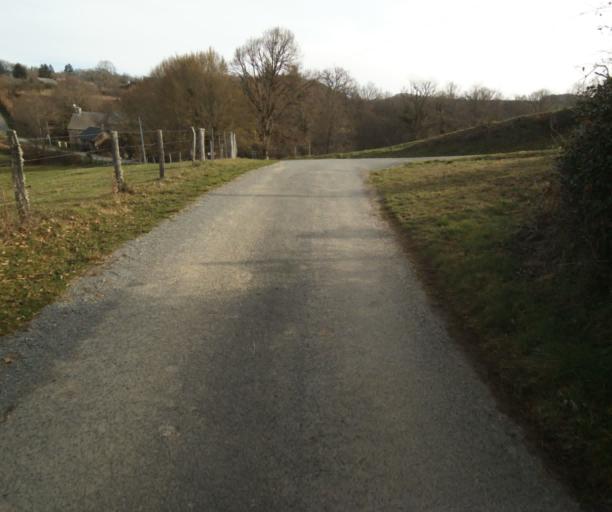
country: FR
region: Limousin
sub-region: Departement de la Correze
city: Chamboulive
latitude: 45.4433
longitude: 1.7538
